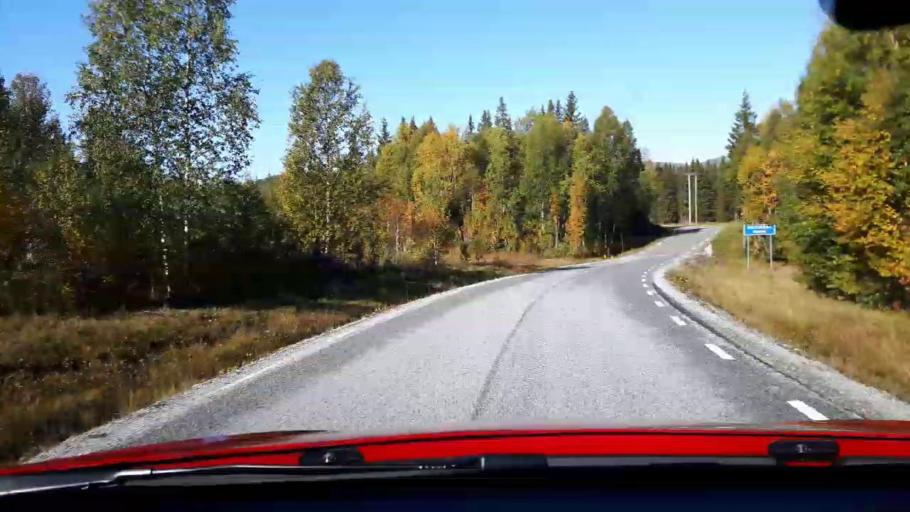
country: NO
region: Nord-Trondelag
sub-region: Lierne
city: Sandvika
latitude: 64.6232
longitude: 13.6927
